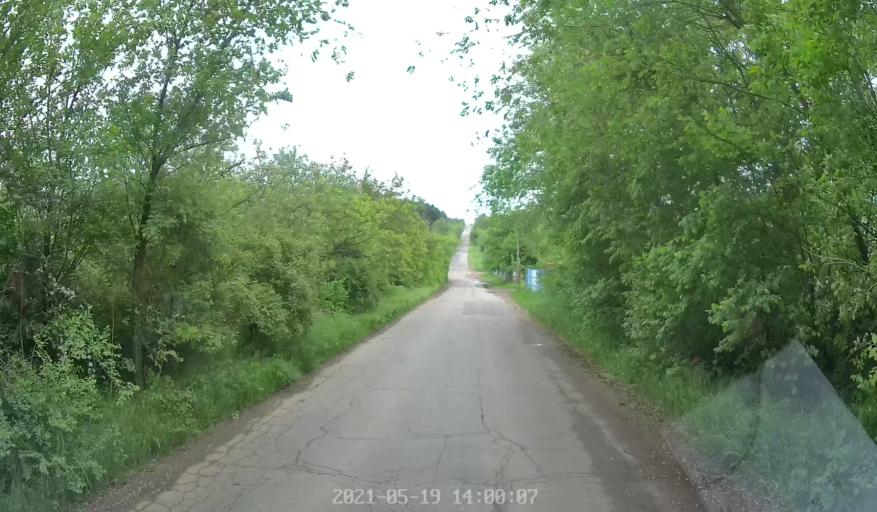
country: MD
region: Chisinau
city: Chisinau
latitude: 47.0365
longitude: 28.9296
